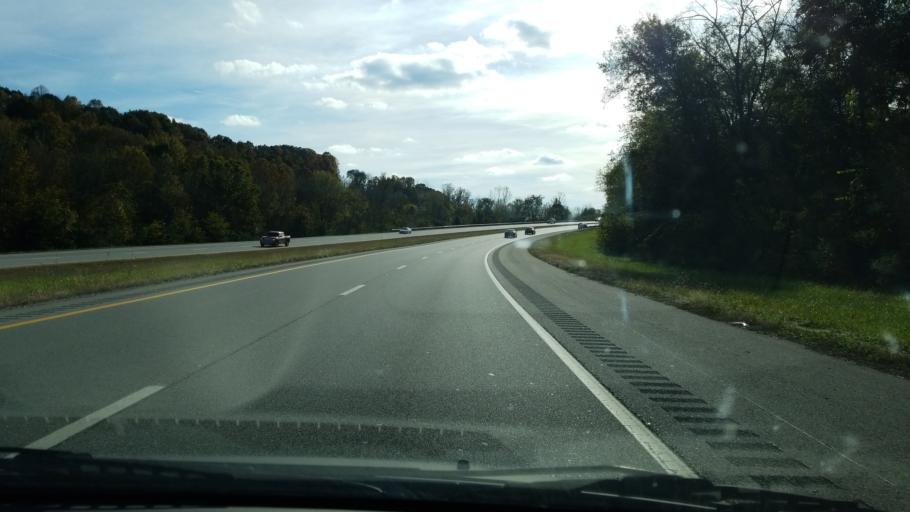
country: US
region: Tennessee
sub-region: Hamilton County
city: Soddy-Daisy
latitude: 35.2417
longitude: -85.1840
